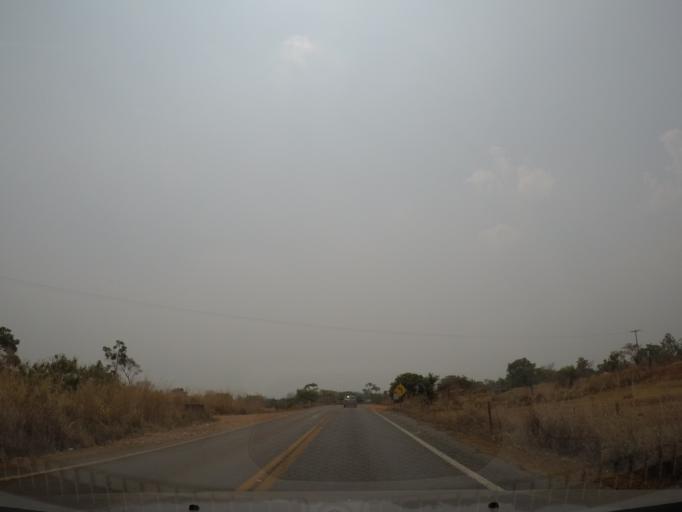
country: BR
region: Goias
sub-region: Pirenopolis
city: Pirenopolis
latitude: -15.8850
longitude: -48.9012
